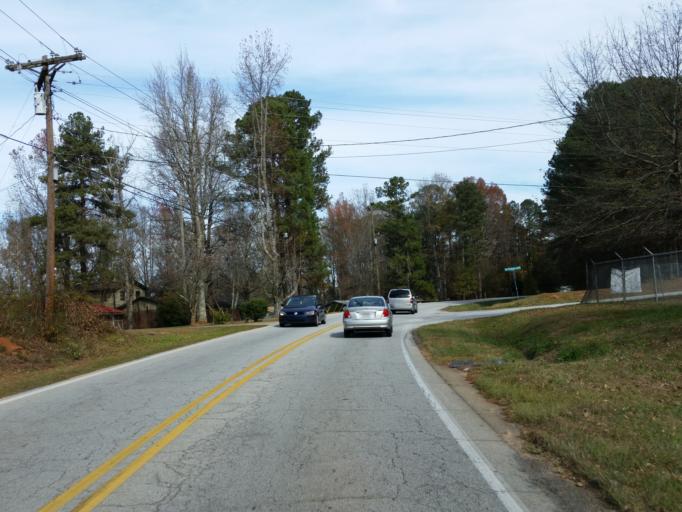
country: US
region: Georgia
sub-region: Douglas County
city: Lithia Springs
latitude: 33.7466
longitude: -84.6622
